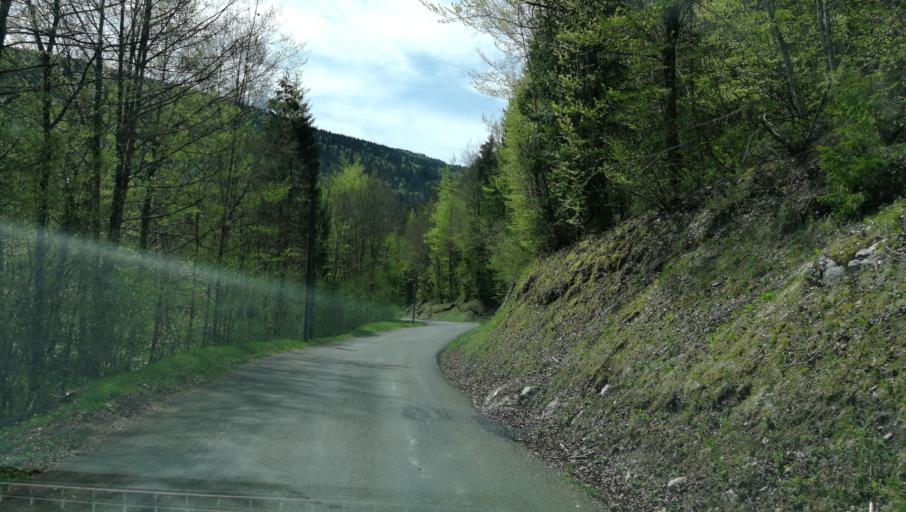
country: FR
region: Rhone-Alpes
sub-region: Departement de l'Ain
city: Chatillon-en-Michaille
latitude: 46.2120
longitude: 5.7484
